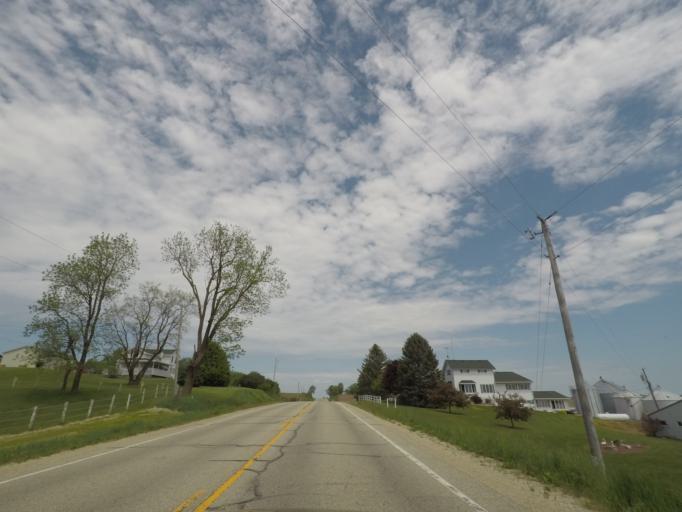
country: US
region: Wisconsin
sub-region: Rock County
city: Orfordville
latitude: 42.6813
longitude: -89.2881
